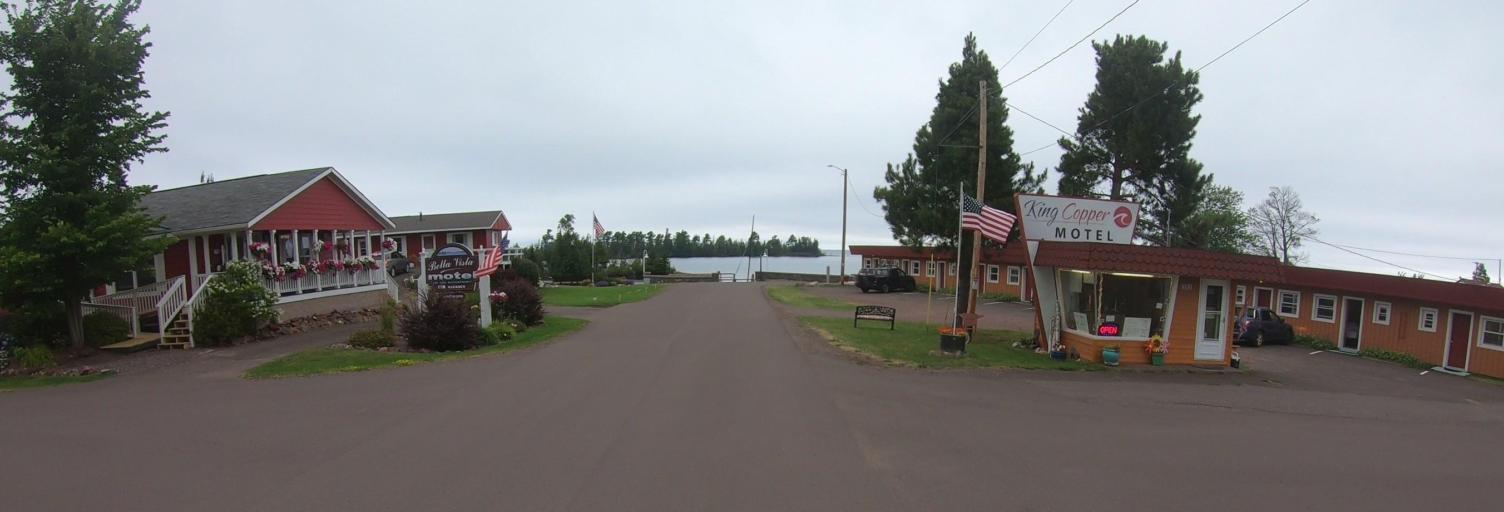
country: US
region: Michigan
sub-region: Keweenaw County
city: Eagle River
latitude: 47.4695
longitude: -87.8927
